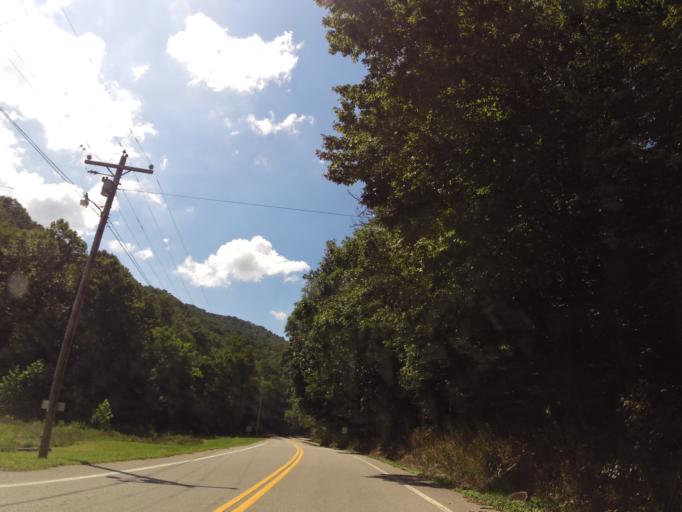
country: US
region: Tennessee
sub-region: Cumberland County
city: Fairfield Glade
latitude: 35.8866
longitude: -84.8378
